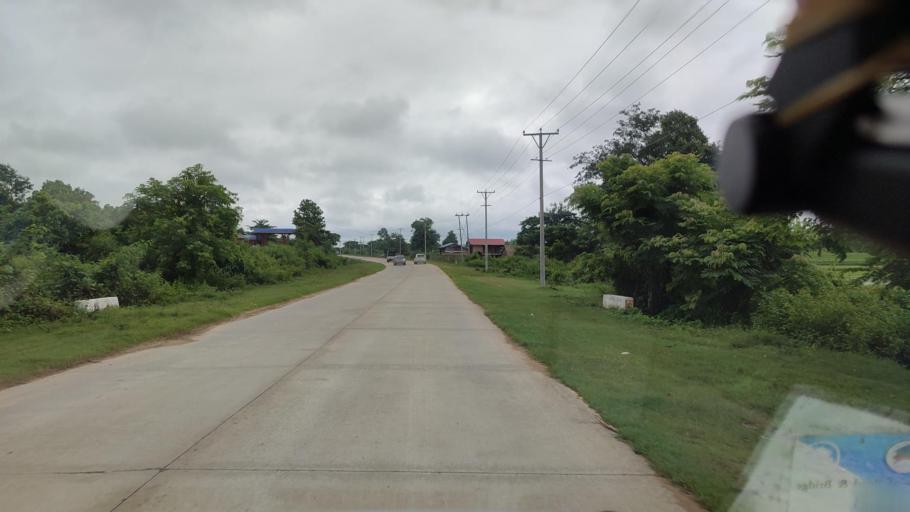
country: MM
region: Mandalay
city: Nay Pyi Taw
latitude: 19.8790
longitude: 96.0248
